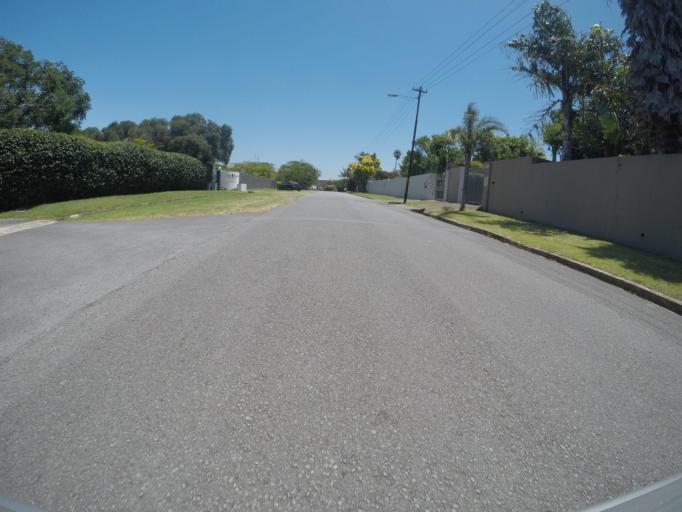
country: ZA
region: Eastern Cape
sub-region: Buffalo City Metropolitan Municipality
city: East London
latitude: -32.9875
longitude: 27.9001
